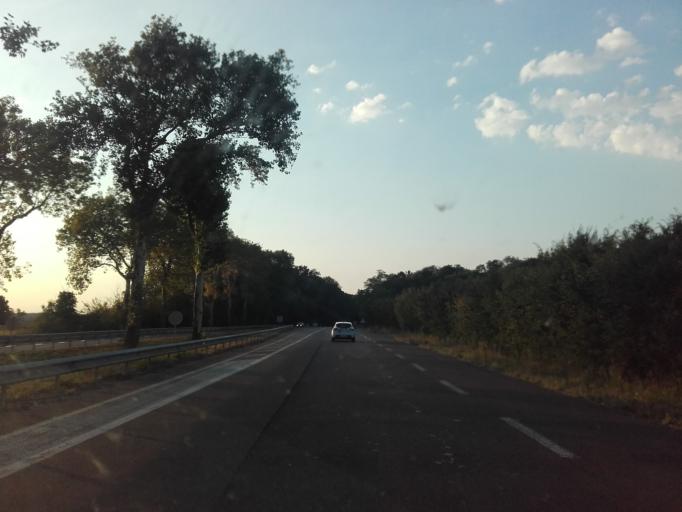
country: FR
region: Bourgogne
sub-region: Departement de l'Yonne
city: Auxerre
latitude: 47.8275
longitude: 3.5550
